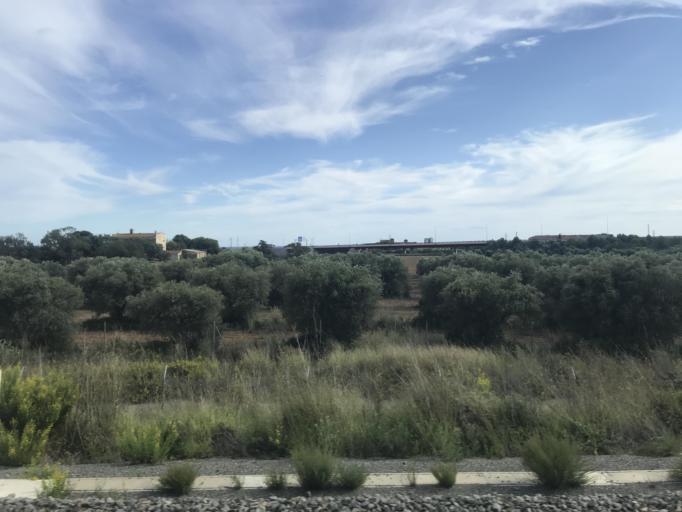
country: ES
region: Catalonia
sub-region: Provincia de Tarragona
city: Cambrils
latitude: 41.0875
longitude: 1.0656
